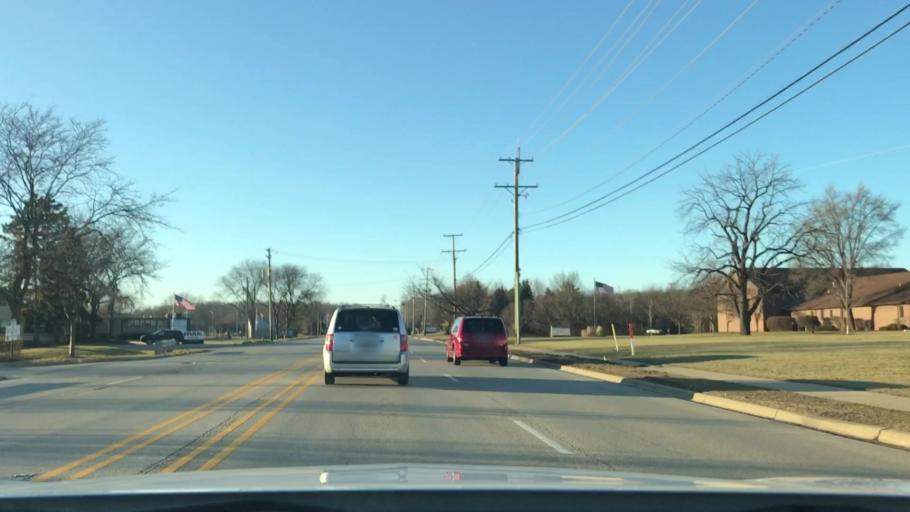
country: US
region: Illinois
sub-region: Kane County
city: Sleepy Hollow
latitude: 42.0595
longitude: -88.3239
